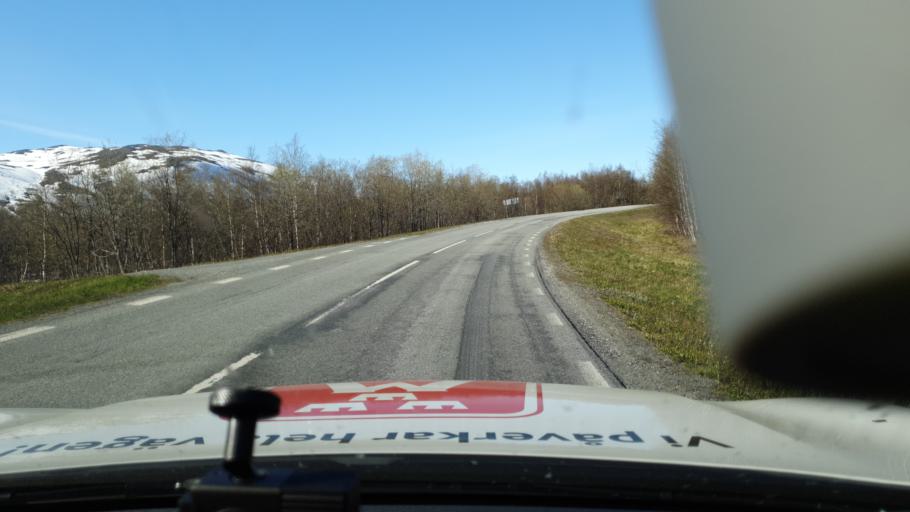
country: NO
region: Nordland
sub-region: Rana
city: Mo i Rana
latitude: 65.9574
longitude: 15.0332
